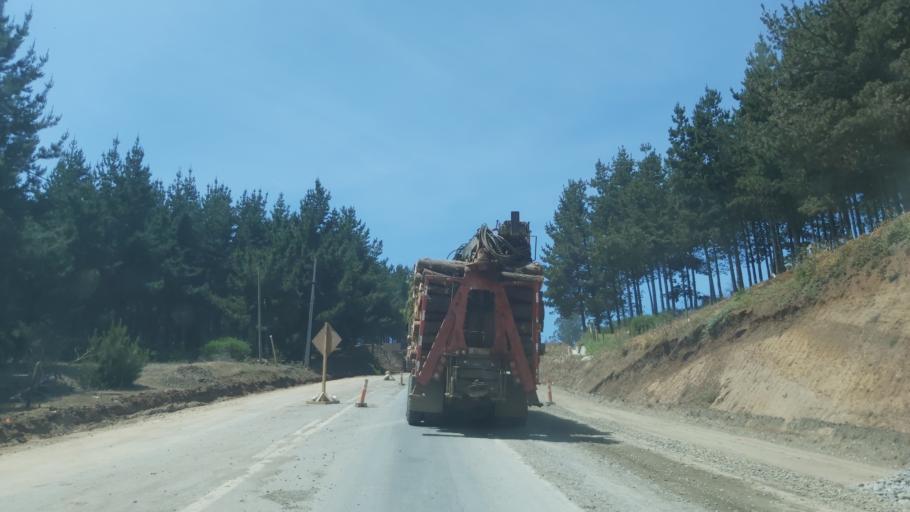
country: CL
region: Maule
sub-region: Provincia de Talca
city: Constitucion
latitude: -35.4494
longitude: -72.4762
